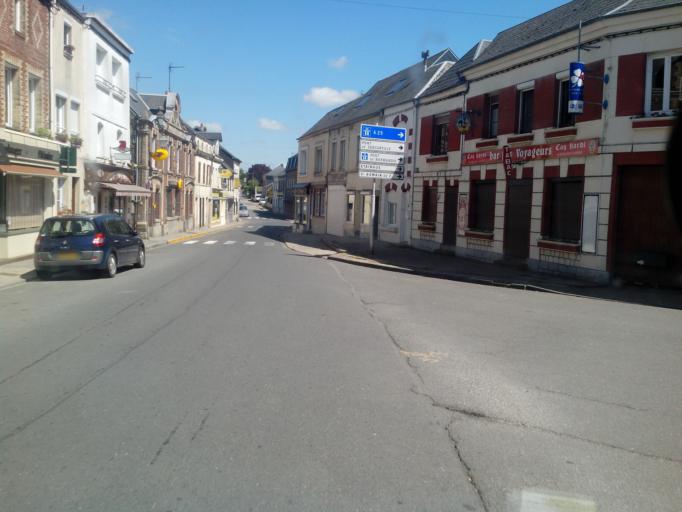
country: FR
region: Haute-Normandie
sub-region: Departement de la Seine-Maritime
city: Maneglise
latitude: 49.5885
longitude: 0.2822
